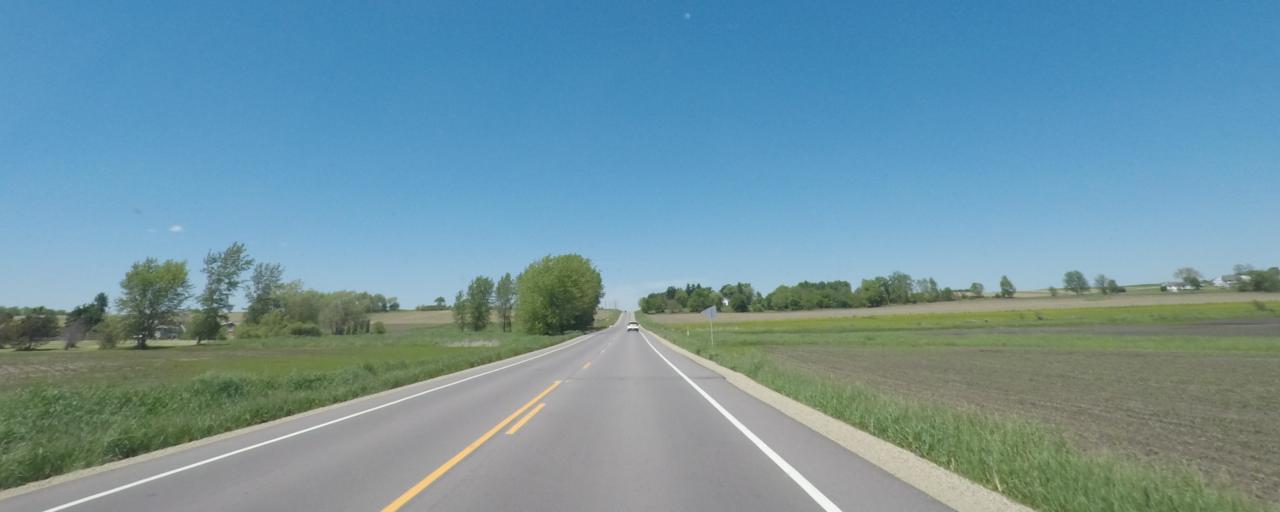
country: US
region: Wisconsin
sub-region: Green County
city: Brooklyn
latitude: 42.8185
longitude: -89.3693
